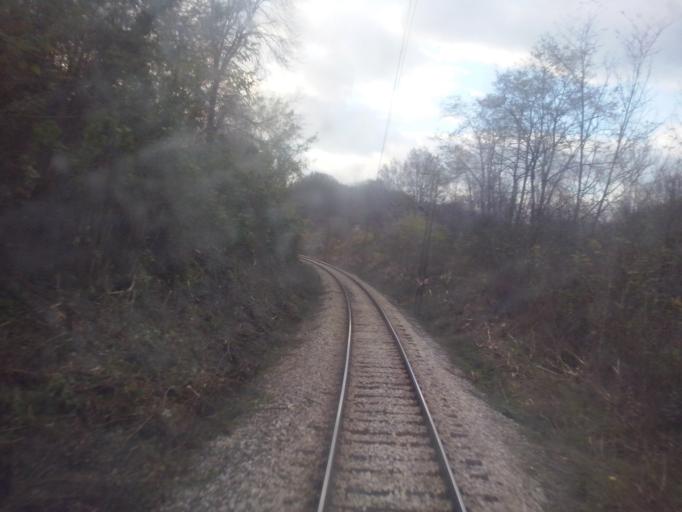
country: RS
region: Central Serbia
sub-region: Zlatiborski Okrug
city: Kosjeric
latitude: 43.9579
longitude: 19.9785
